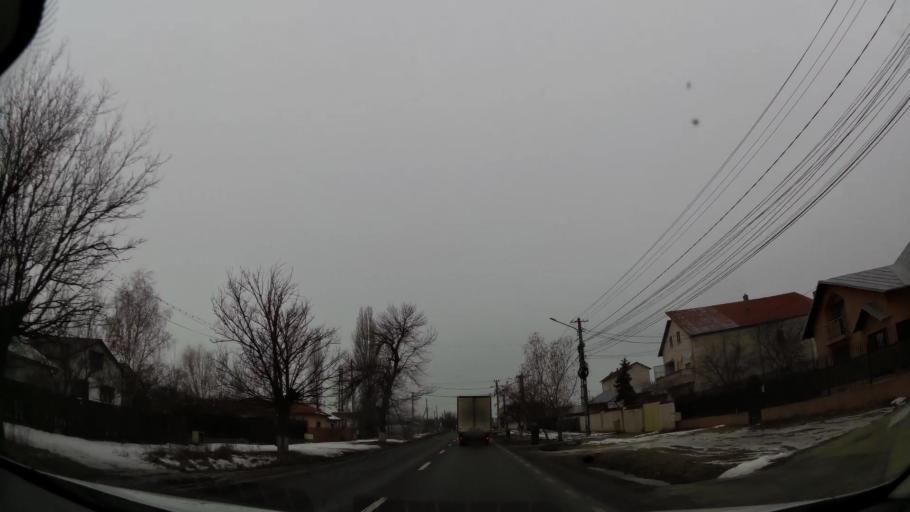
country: RO
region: Dambovita
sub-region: Comuna Racari
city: Racari
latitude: 44.6197
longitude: 25.7553
